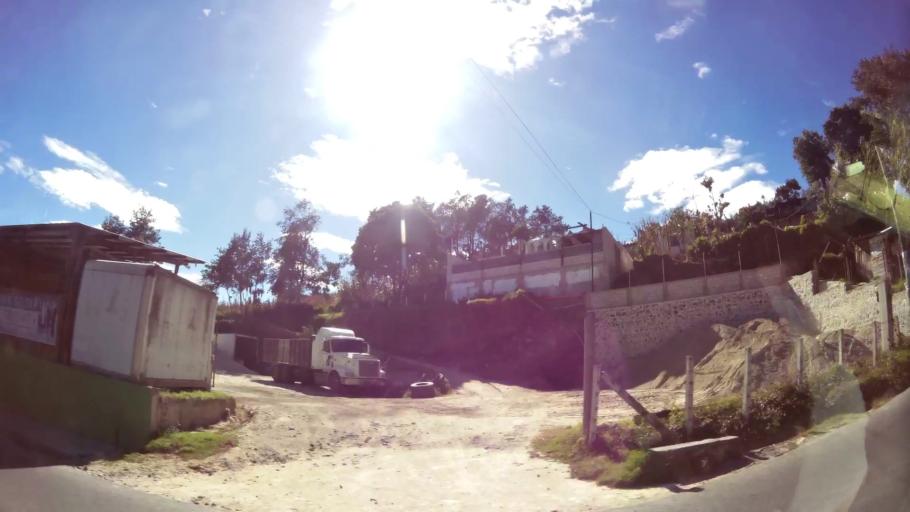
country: GT
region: Solola
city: Solola
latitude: 14.7851
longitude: -91.1828
